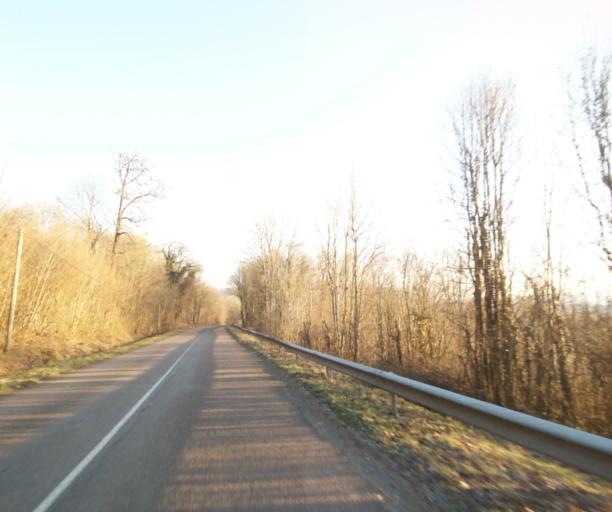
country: FR
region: Champagne-Ardenne
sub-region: Departement de la Haute-Marne
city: Chevillon
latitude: 48.5473
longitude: 5.0980
